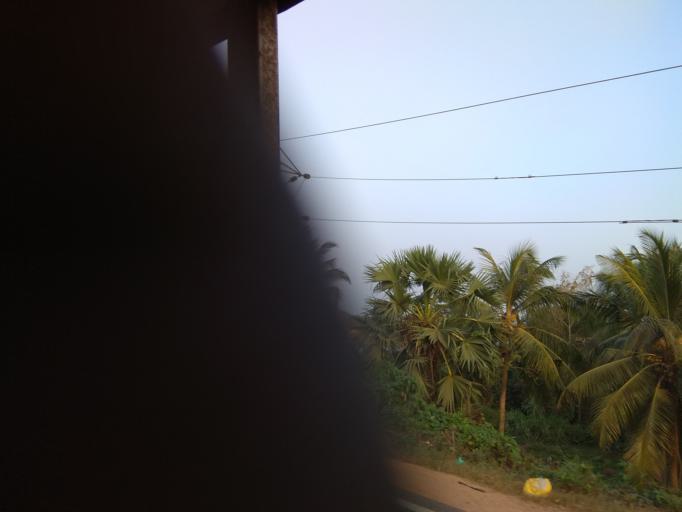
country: IN
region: Karnataka
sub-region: Dakshina Kannada
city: Mangalore
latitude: 12.9400
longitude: 74.8652
